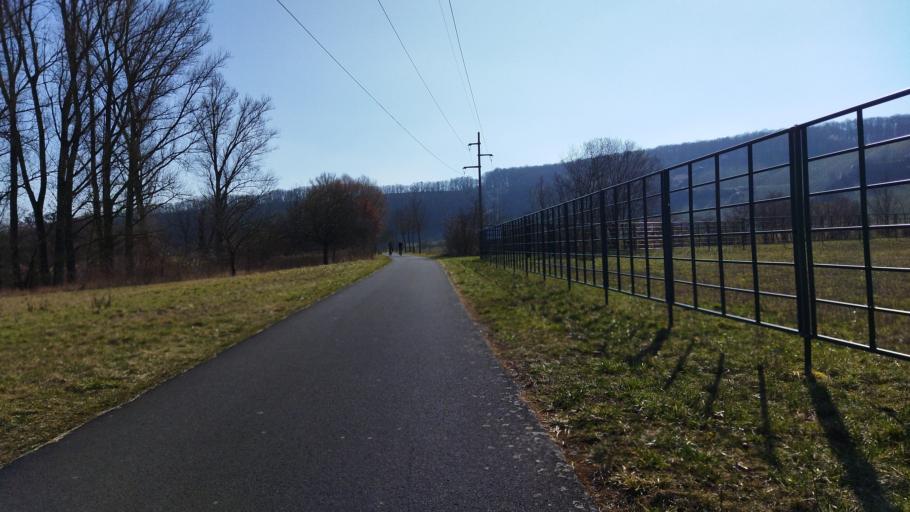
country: DE
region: Bavaria
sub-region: Regierungsbezirk Unterfranken
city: Marktsteft
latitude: 49.6940
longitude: 10.1290
